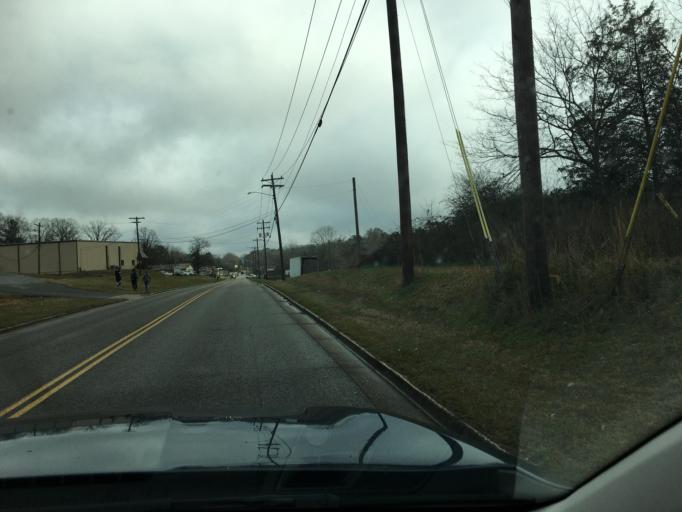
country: US
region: Tennessee
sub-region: McMinn County
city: Athens
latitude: 35.4392
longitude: -84.6251
